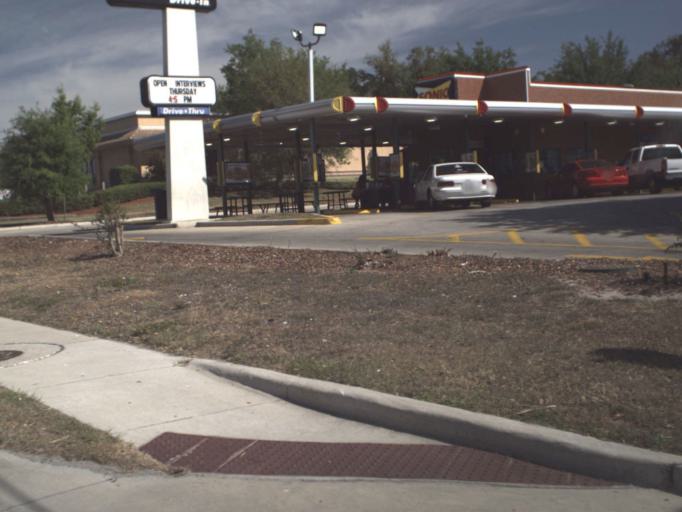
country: US
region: Florida
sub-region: Lake County
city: Leesburg
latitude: 28.8361
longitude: -81.8906
